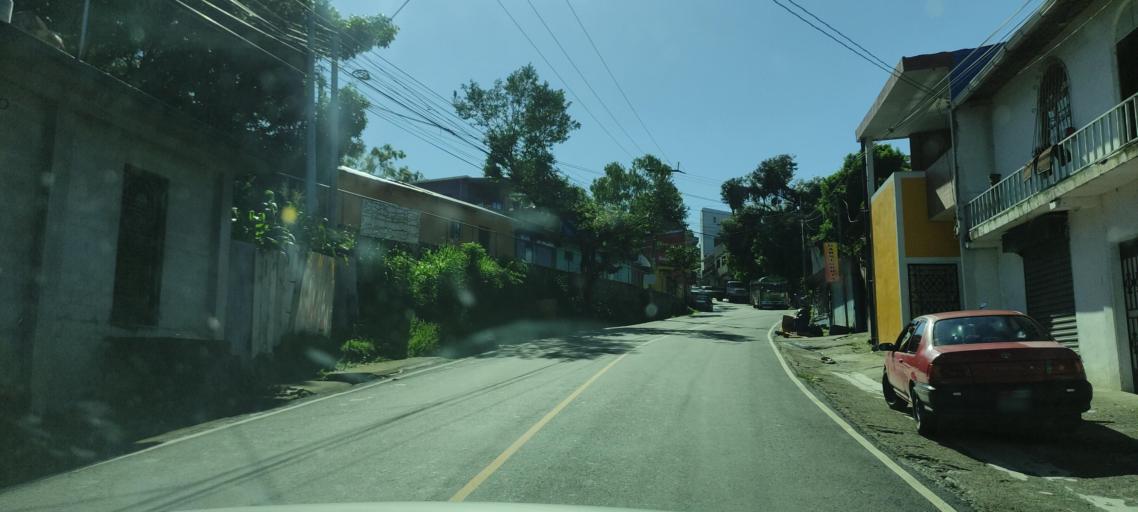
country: HN
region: Ocotepeque
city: Antigua Ocotepeque
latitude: 14.3184
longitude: -89.1721
